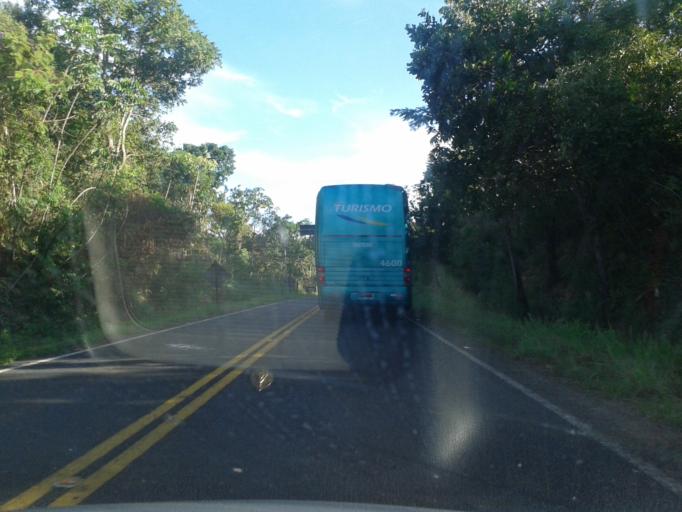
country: BR
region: Minas Gerais
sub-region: Tupaciguara
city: Tupaciguara
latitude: -18.3118
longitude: -48.5618
